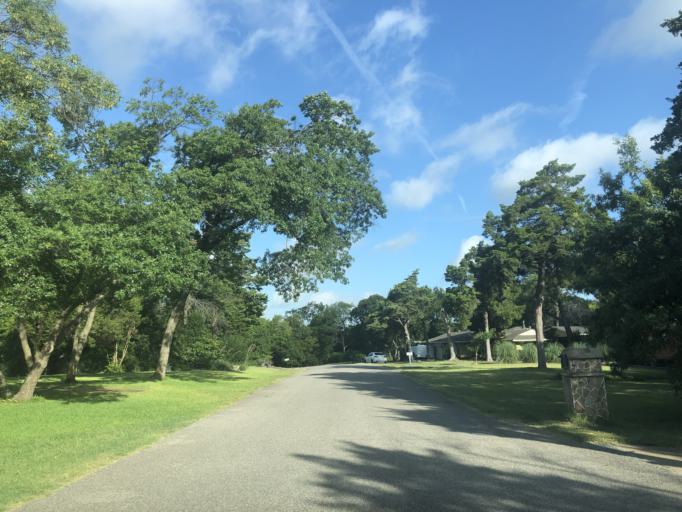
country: US
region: Texas
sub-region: Dallas County
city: Duncanville
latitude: 32.6664
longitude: -96.9206
